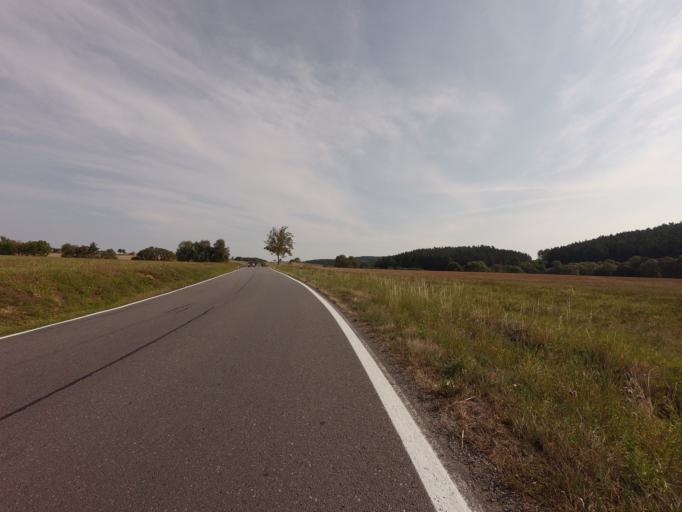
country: CZ
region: Jihocesky
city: Milevsko
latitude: 49.4739
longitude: 14.3642
